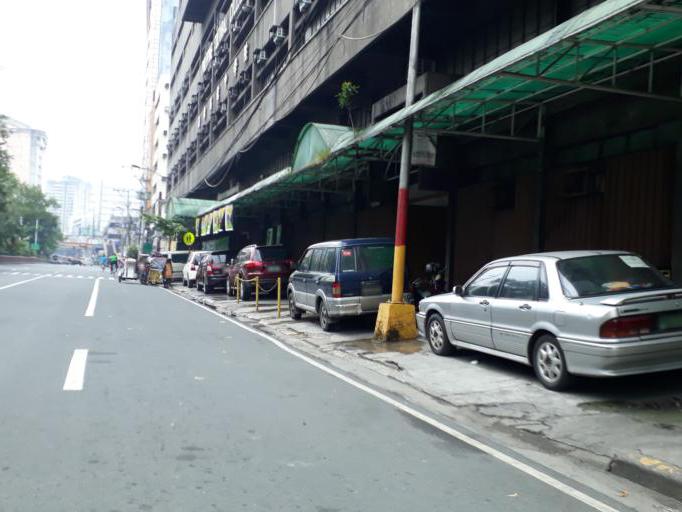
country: PH
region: Metro Manila
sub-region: City of Manila
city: Manila
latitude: 14.6080
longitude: 120.9755
